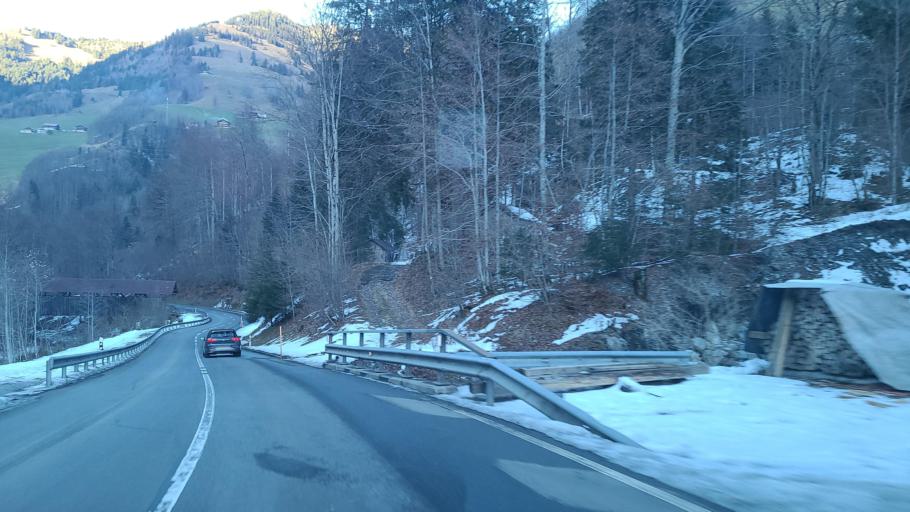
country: CH
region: Obwalden
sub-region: Obwalden
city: Kerns
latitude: 46.8469
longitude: 8.2969
